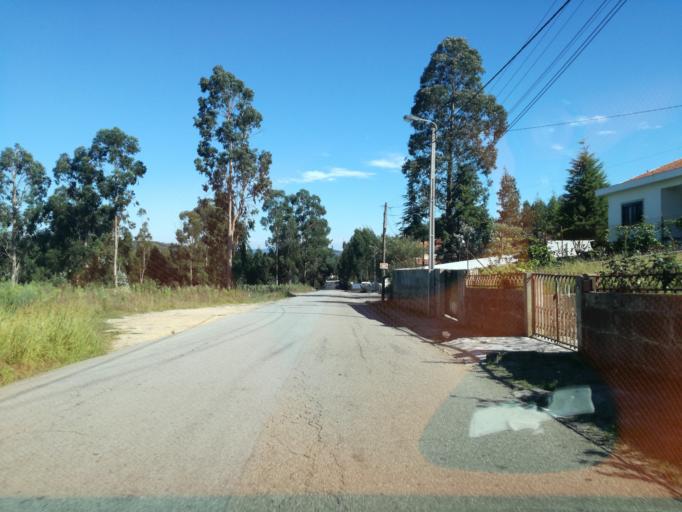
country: PT
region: Porto
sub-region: Trofa
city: Sao Romao do Coronado
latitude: 41.2731
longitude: -8.5389
